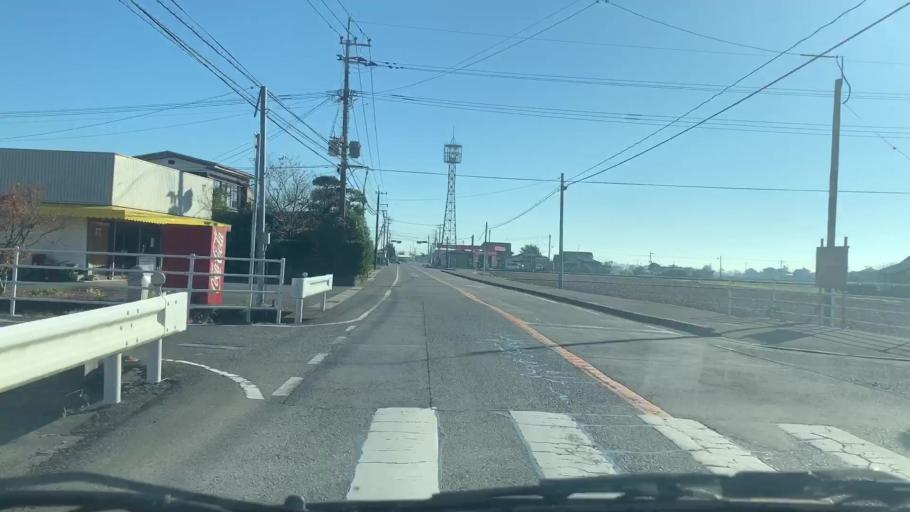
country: JP
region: Saga Prefecture
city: Kashima
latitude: 33.1827
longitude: 130.1798
